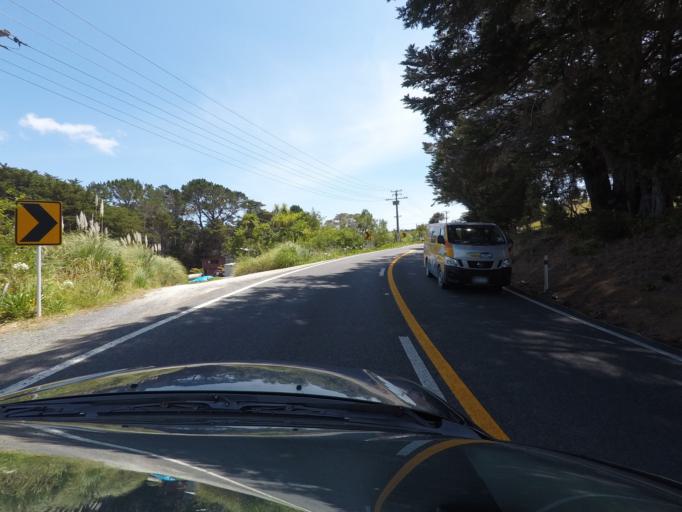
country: NZ
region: Auckland
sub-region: Auckland
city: Warkworth
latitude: -36.3041
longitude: 174.7896
